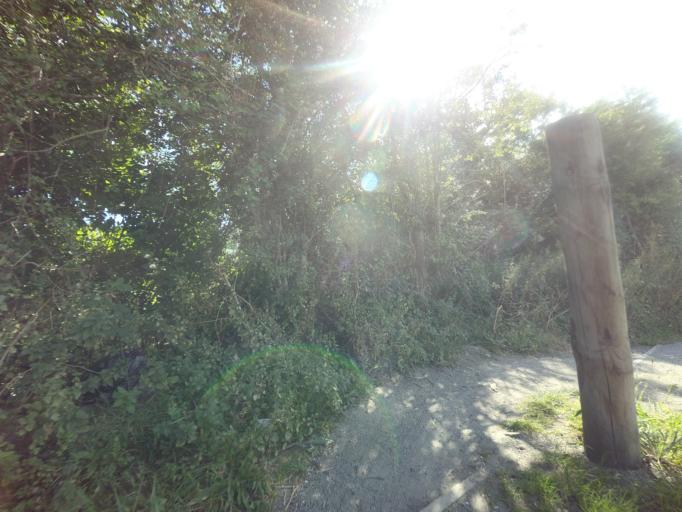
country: GB
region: England
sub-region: Kent
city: Birchington-on-Sea
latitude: 51.3614
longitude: 1.2244
